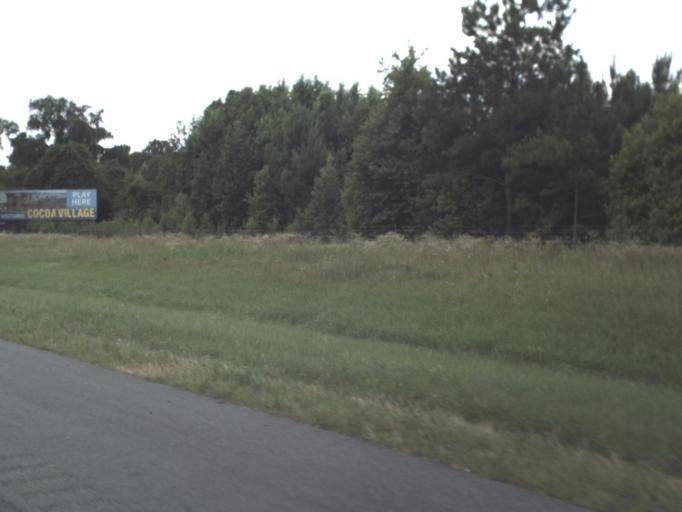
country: US
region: Florida
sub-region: Hamilton County
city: Jasper
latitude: 30.4005
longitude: -82.8851
